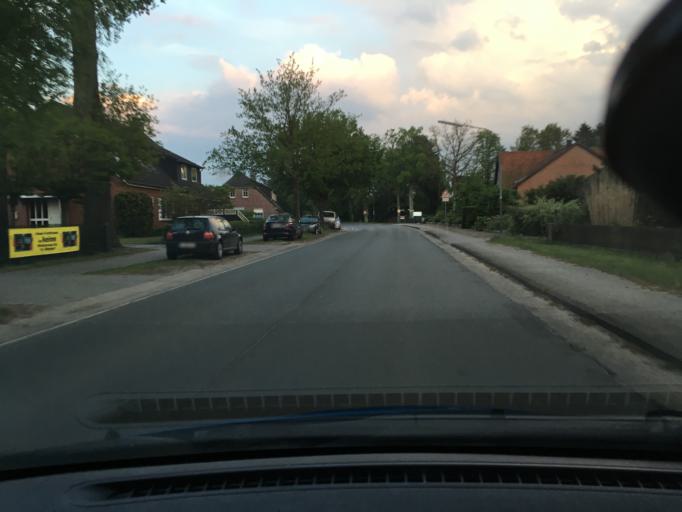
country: DE
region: Lower Saxony
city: Vierhofen
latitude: 53.2666
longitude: 10.2167
